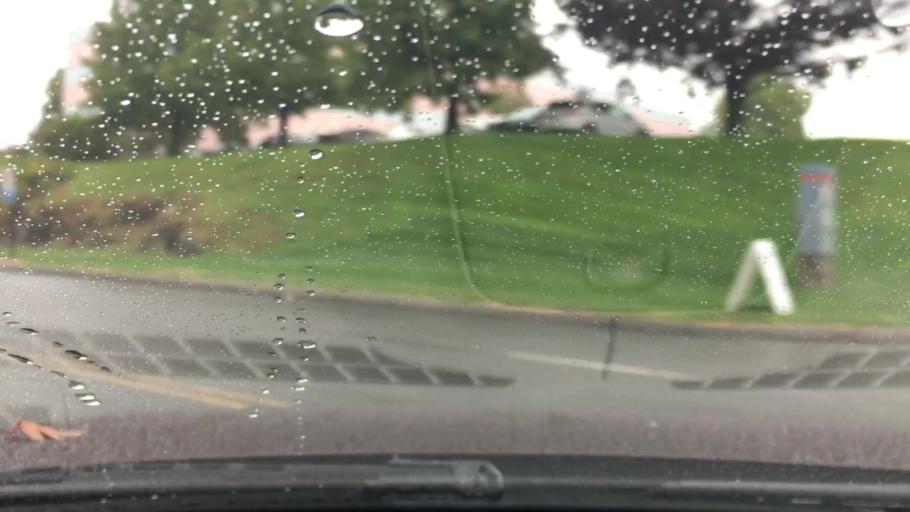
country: US
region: Connecticut
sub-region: Middlesex County
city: Cromwell
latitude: 41.6498
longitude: -72.6673
